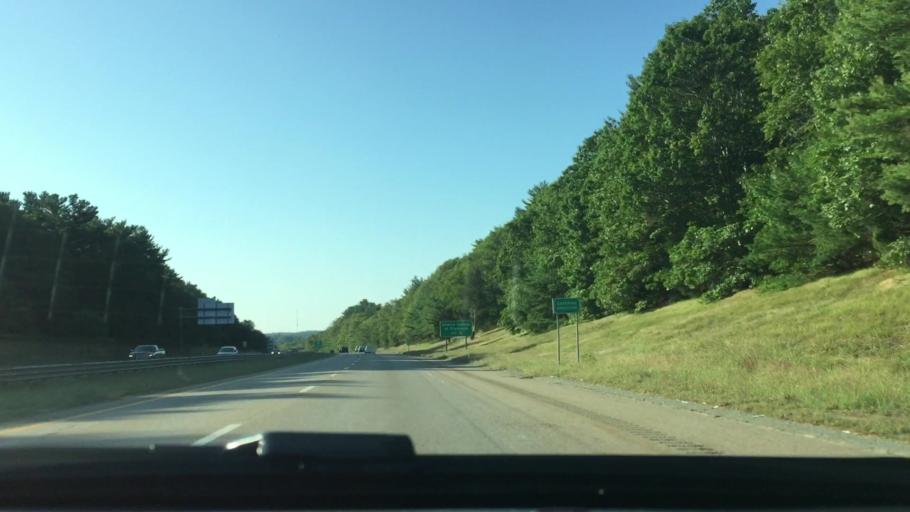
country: US
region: Massachusetts
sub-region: Plymouth County
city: Kingston
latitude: 42.0119
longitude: -70.7266
